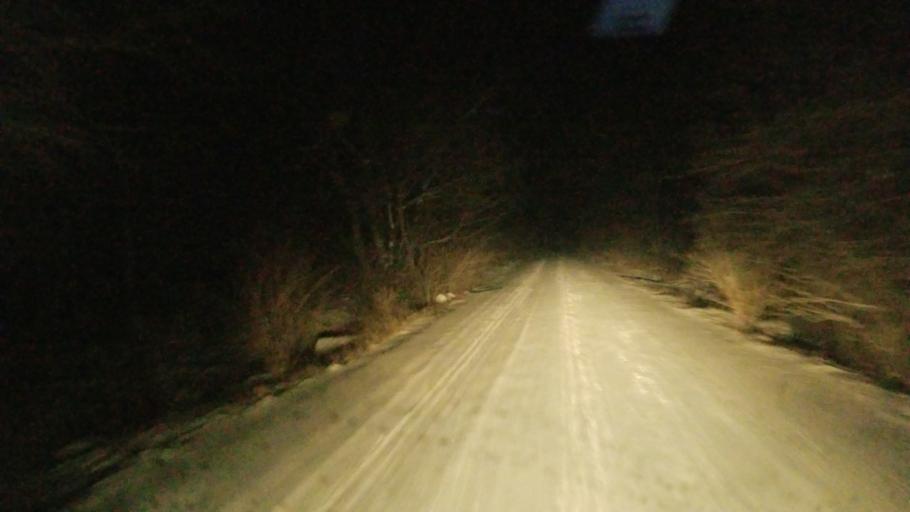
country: US
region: Michigan
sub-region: Osceola County
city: Reed City
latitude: 43.8368
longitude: -85.4141
